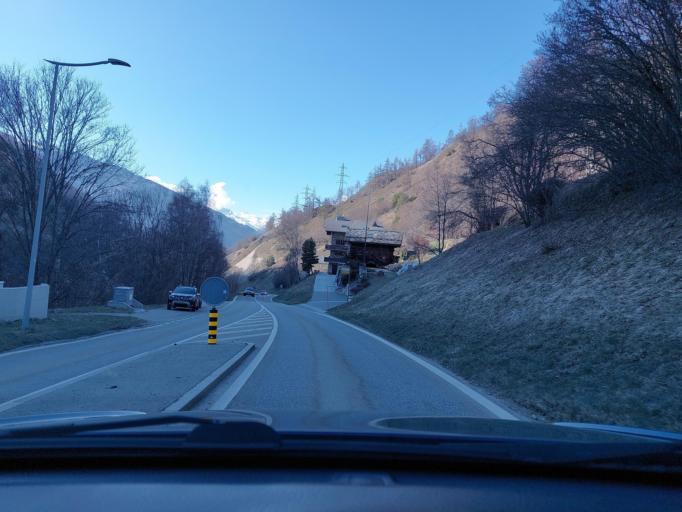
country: CH
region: Valais
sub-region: Herens District
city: Heremence
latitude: 46.1538
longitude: 7.4517
